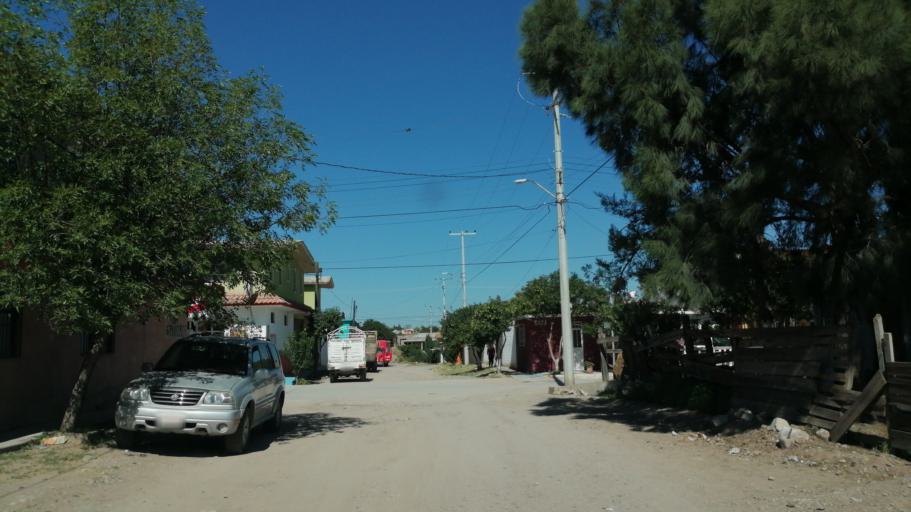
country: MX
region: Durango
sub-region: Santiago Papasquiaro
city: Santiago Papasquiaro
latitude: 25.0498
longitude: -105.4358
